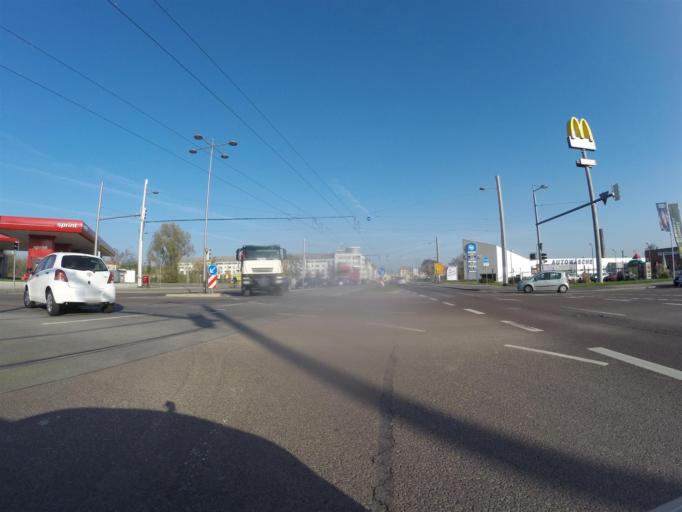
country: DE
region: Saxony
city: Leipzig
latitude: 51.3280
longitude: 12.3091
